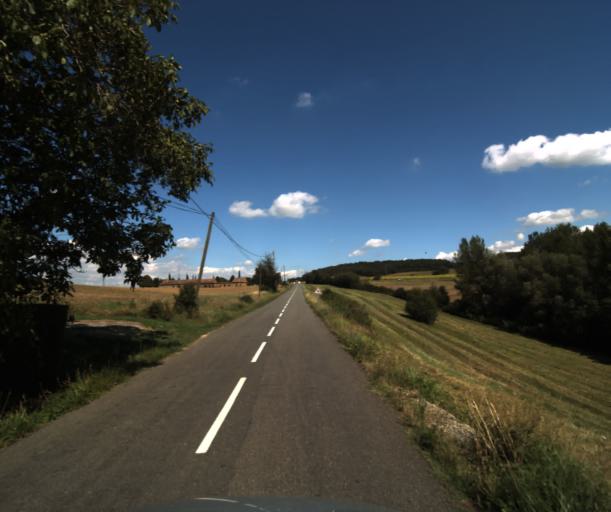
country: FR
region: Midi-Pyrenees
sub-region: Departement de la Haute-Garonne
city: Le Fauga
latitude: 43.4077
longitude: 1.3181
